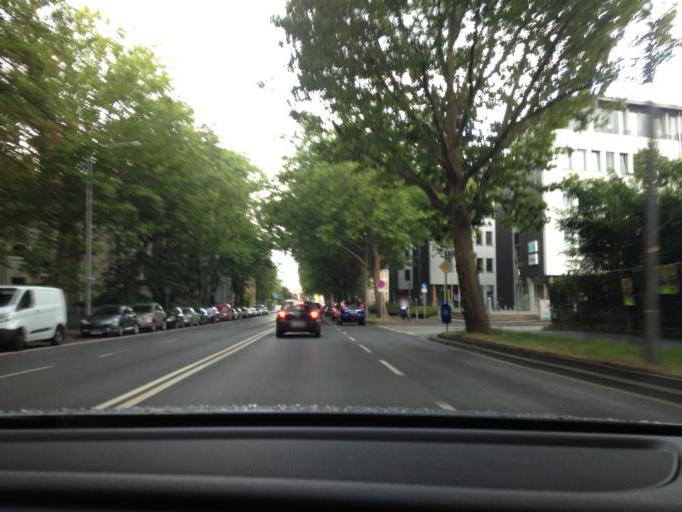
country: DE
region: Hesse
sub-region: Regierungsbezirk Darmstadt
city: Wiesbaden
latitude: 50.0736
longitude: 8.2244
